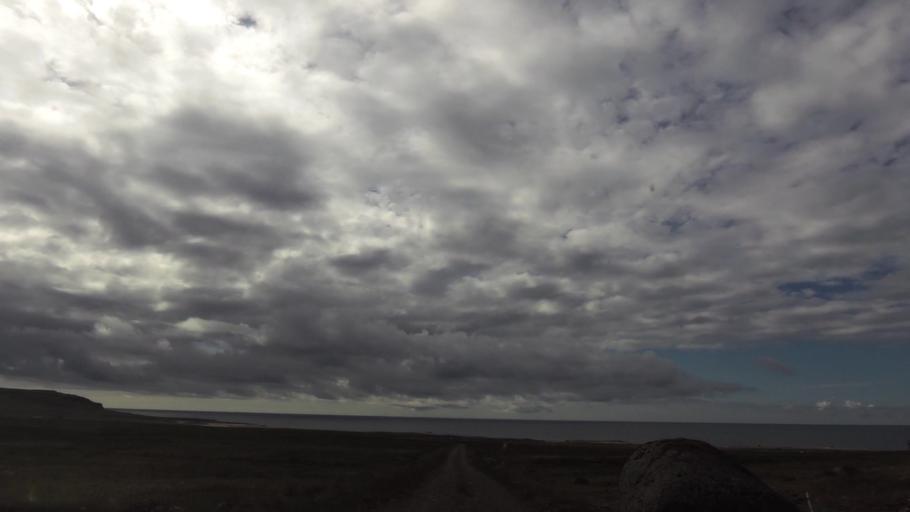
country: IS
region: West
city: Olafsvik
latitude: 65.6141
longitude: -24.3154
